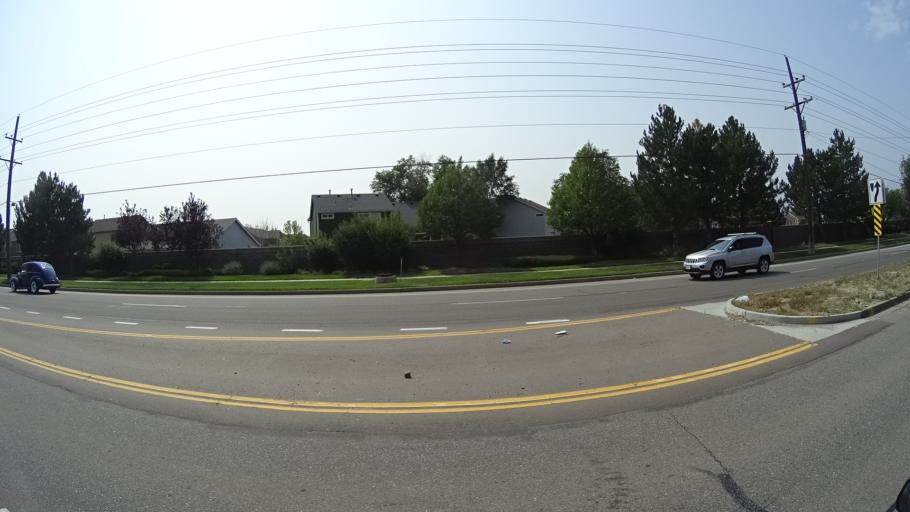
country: US
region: Colorado
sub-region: El Paso County
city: Cimarron Hills
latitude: 38.8251
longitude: -104.7314
